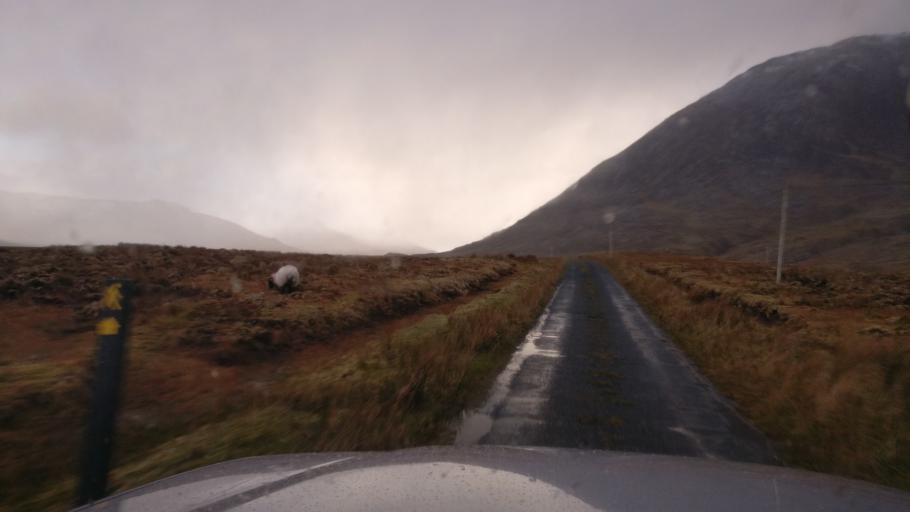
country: IE
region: Connaught
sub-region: County Galway
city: Clifden
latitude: 53.5154
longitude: -9.7166
